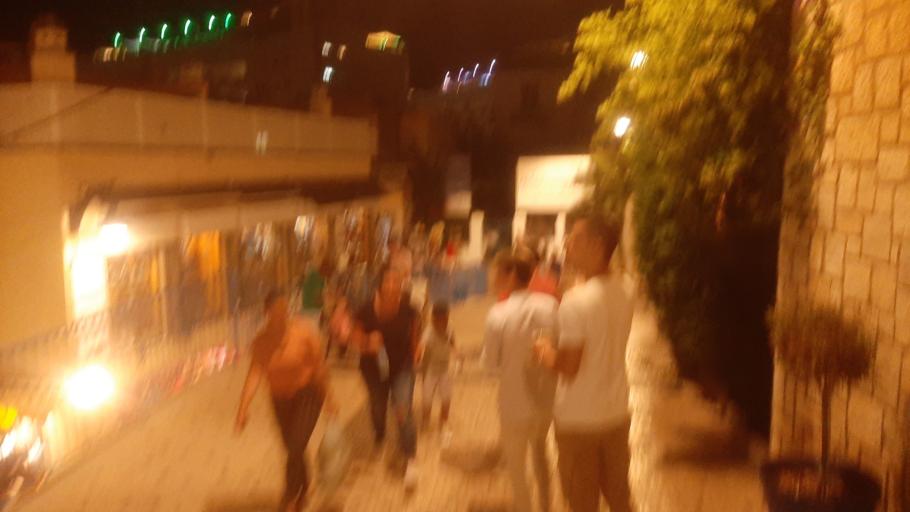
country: ES
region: Andalusia
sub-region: Provincia de Malaga
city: Torremolinos
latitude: 36.6221
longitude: -4.4969
